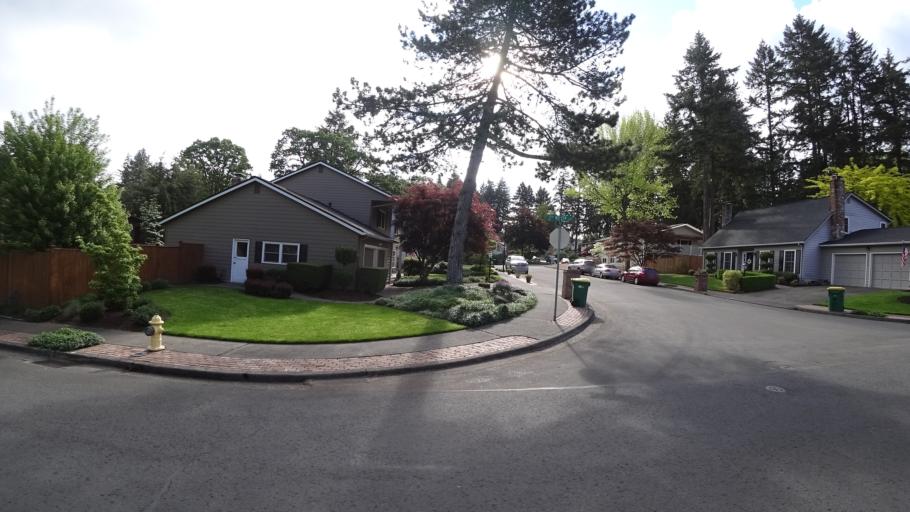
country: US
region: Oregon
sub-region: Washington County
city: Beaverton
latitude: 45.4648
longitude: -122.8182
